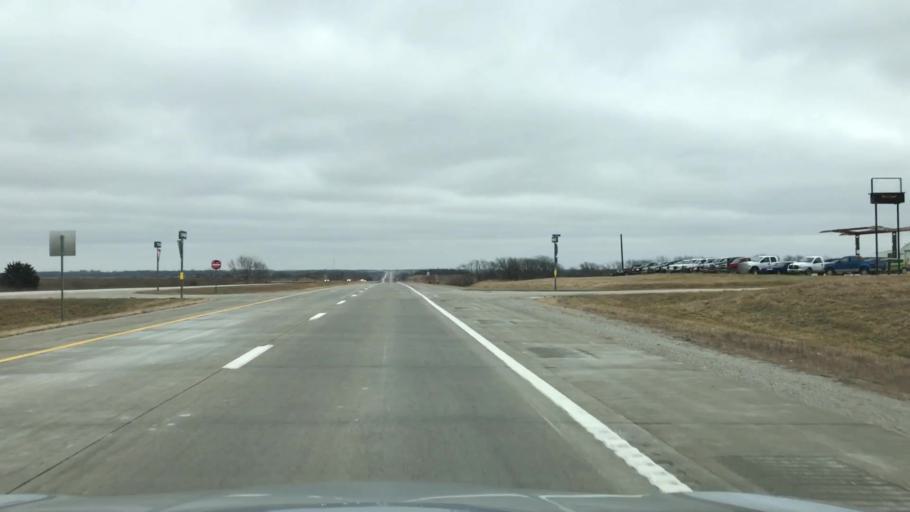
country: US
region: Missouri
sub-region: Caldwell County
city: Hamilton
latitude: 39.7351
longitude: -93.8530
